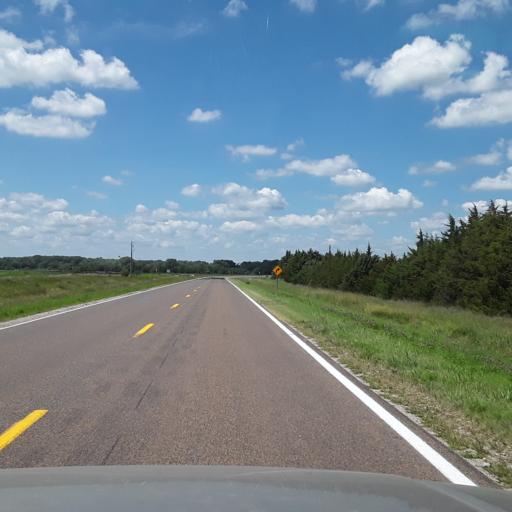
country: US
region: Nebraska
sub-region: Nance County
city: Genoa
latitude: 41.4066
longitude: -97.7123
